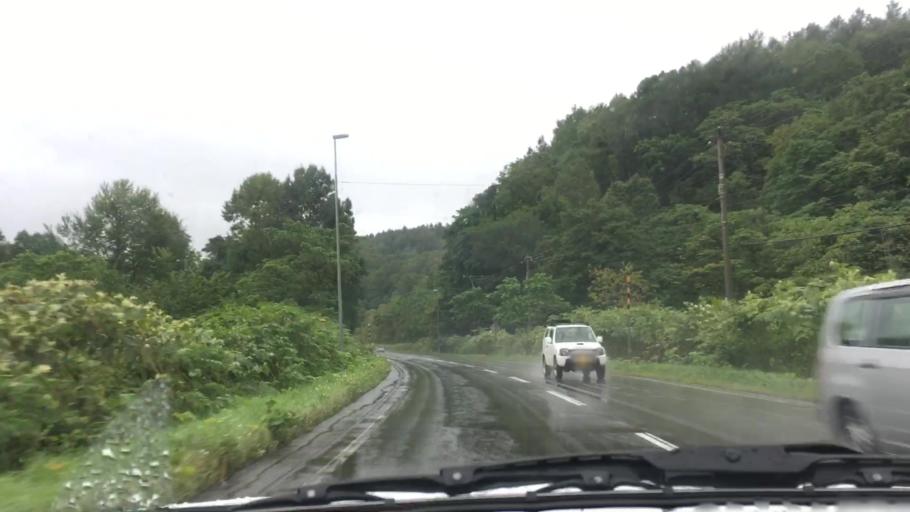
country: JP
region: Hokkaido
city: Niseko Town
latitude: 42.8231
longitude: 141.0032
